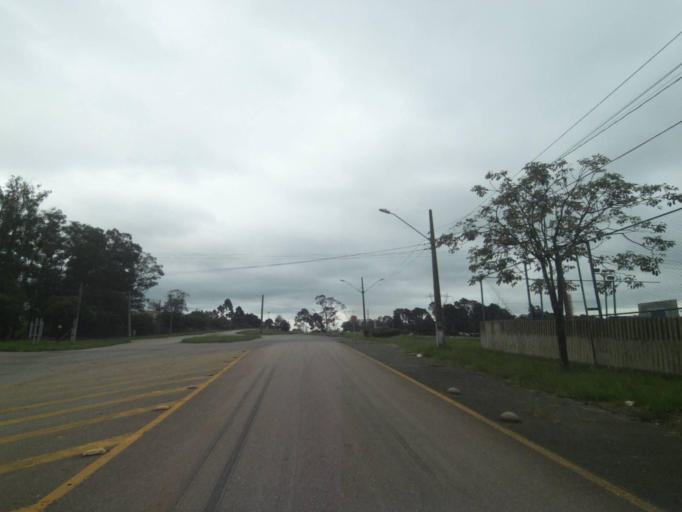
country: BR
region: Parana
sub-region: Araucaria
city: Araucaria
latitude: -25.5458
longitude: -49.3158
